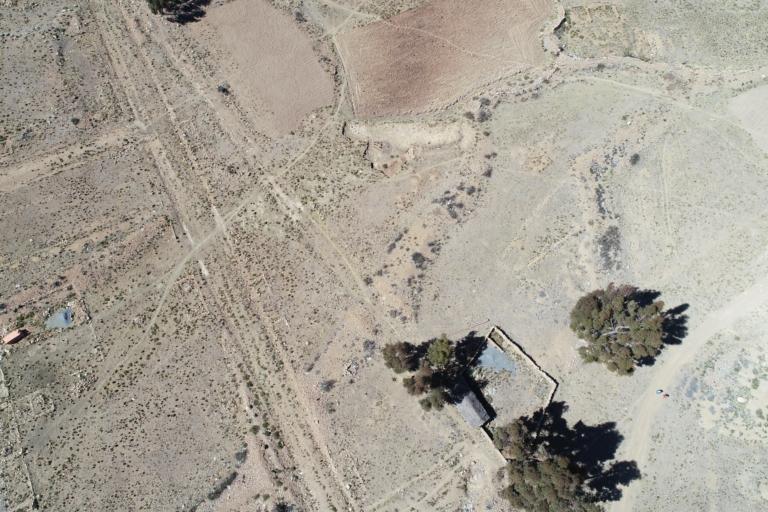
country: BO
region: La Paz
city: Achacachi
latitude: -15.8878
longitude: -68.8125
